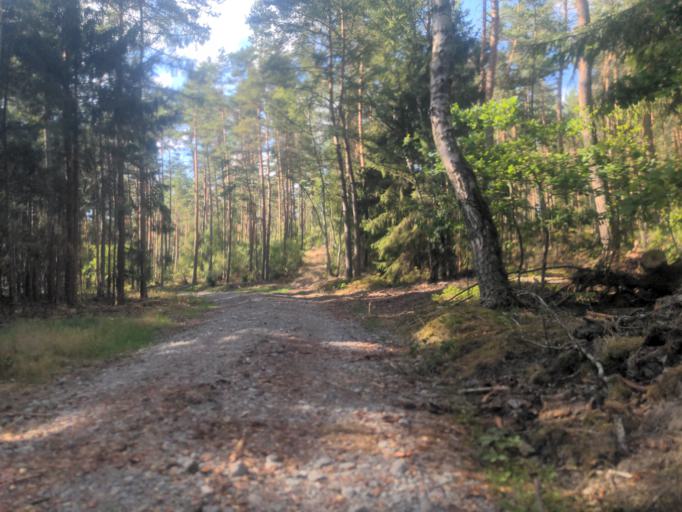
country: DE
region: Lower Saxony
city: Tosterglope
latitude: 53.2041
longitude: 10.8450
